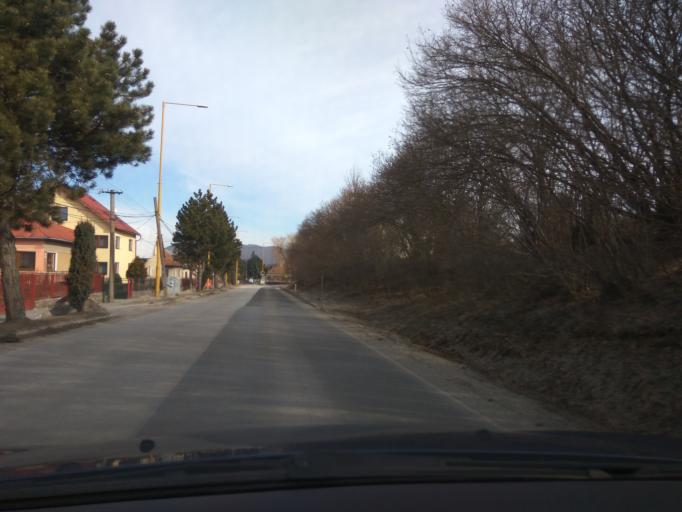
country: SK
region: Zilinsky
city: Rajec
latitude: 49.0900
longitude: 18.6286
